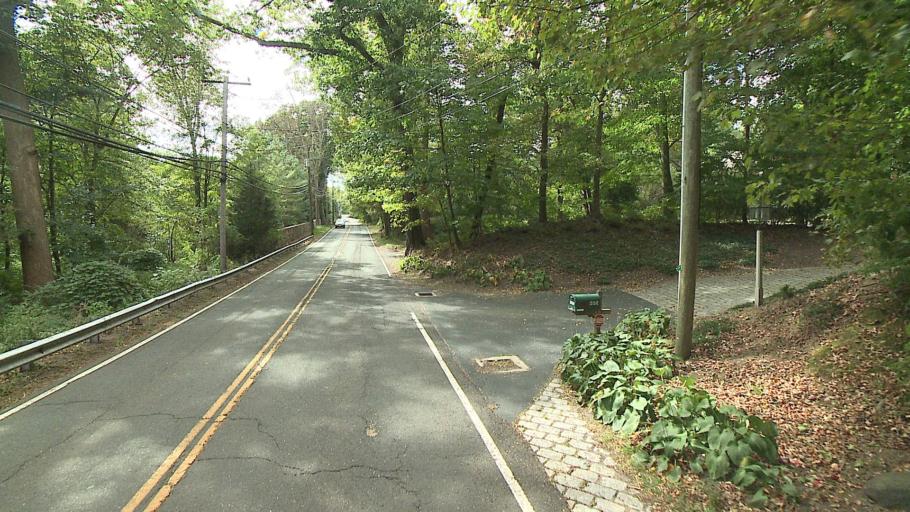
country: US
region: Connecticut
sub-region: Fairfield County
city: New Canaan
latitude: 41.1553
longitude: -73.4767
